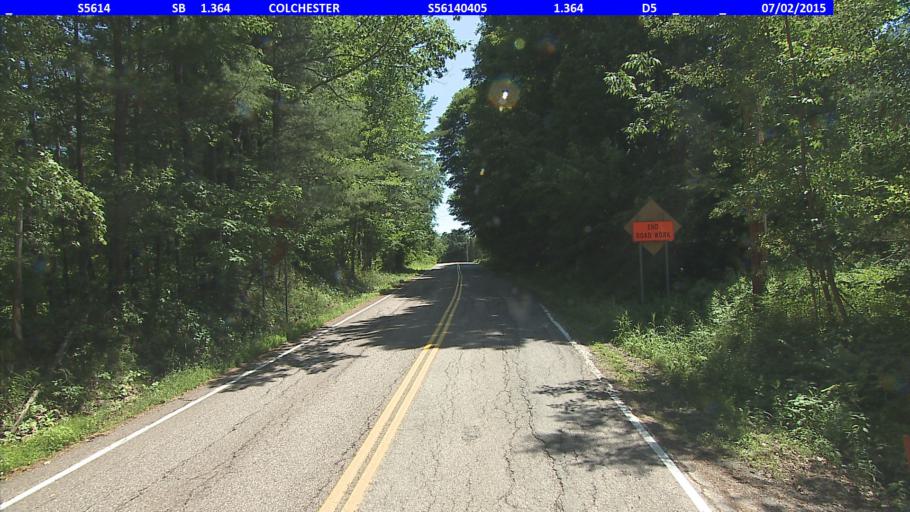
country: US
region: Vermont
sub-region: Chittenden County
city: Colchester
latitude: 44.5384
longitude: -73.1537
